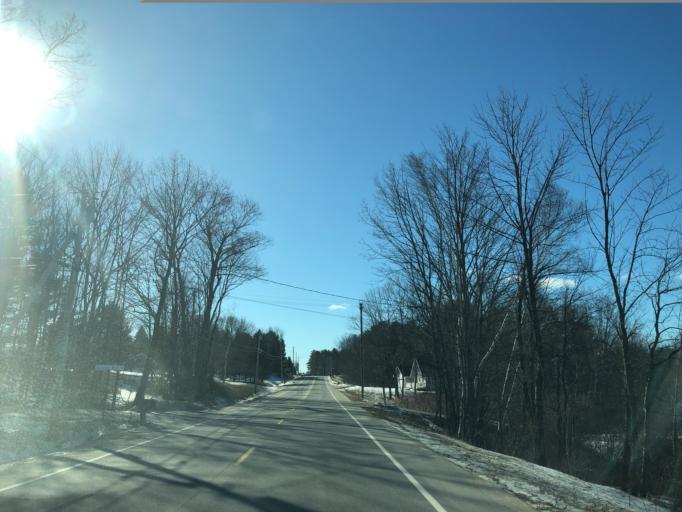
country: US
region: Maine
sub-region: Cumberland County
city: South Windham
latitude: 43.7776
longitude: -70.4396
